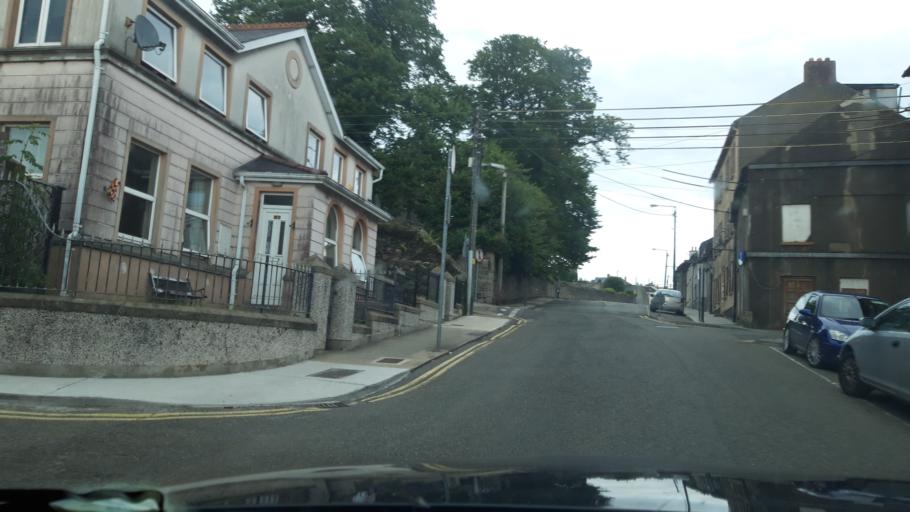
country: IE
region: Leinster
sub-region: Loch Garman
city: New Ross
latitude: 52.3955
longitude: -6.9413
